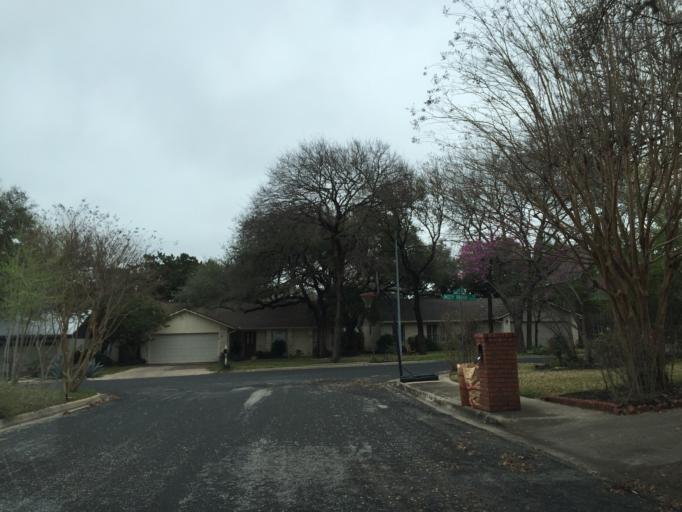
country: US
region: Texas
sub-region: Williamson County
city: Jollyville
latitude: 30.4174
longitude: -97.7335
